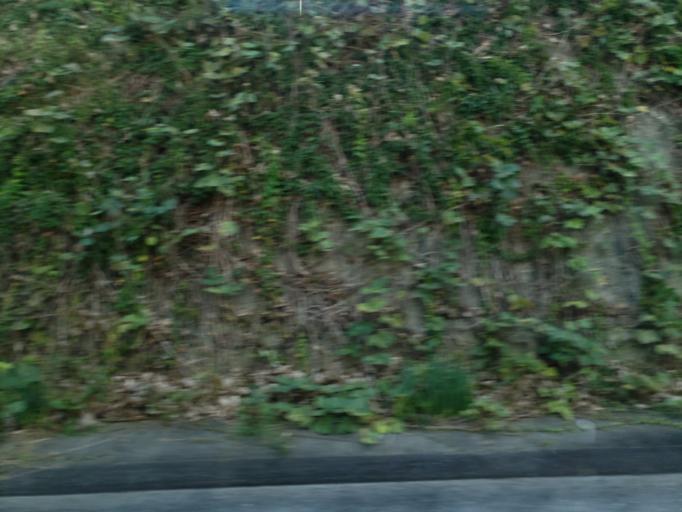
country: JP
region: Tokushima
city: Ishii
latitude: 34.1422
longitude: 134.4215
